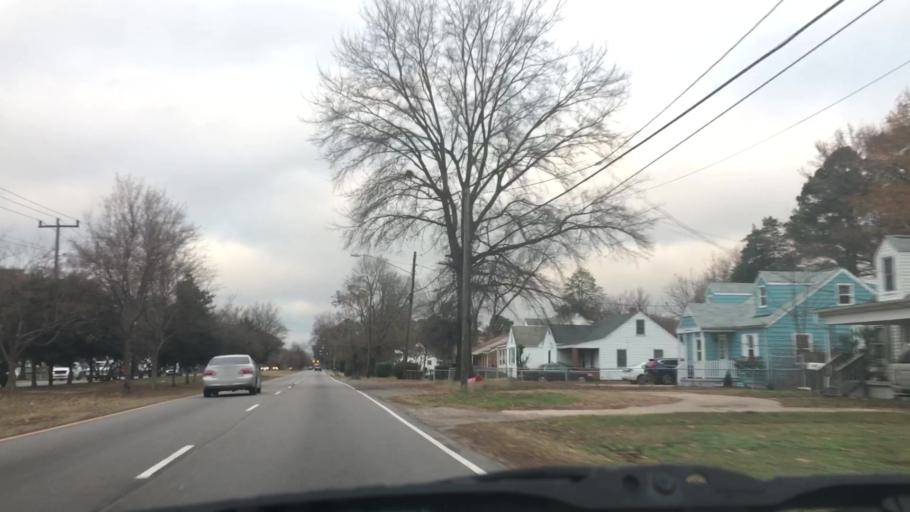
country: US
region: Virginia
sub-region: City of Norfolk
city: Norfolk
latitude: 36.9181
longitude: -76.2419
